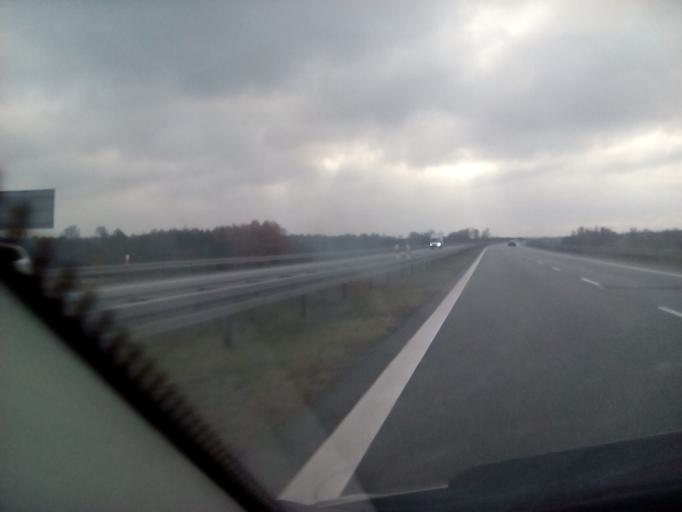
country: PL
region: Masovian Voivodeship
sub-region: Powiat bialobrzeski
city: Bialobrzegi
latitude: 51.6598
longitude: 20.9622
